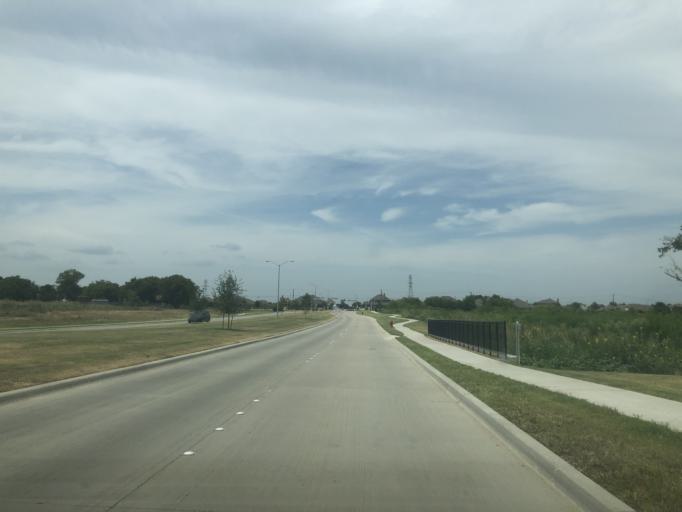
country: US
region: Texas
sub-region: Tarrant County
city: Saginaw
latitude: 32.8809
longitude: -97.3550
